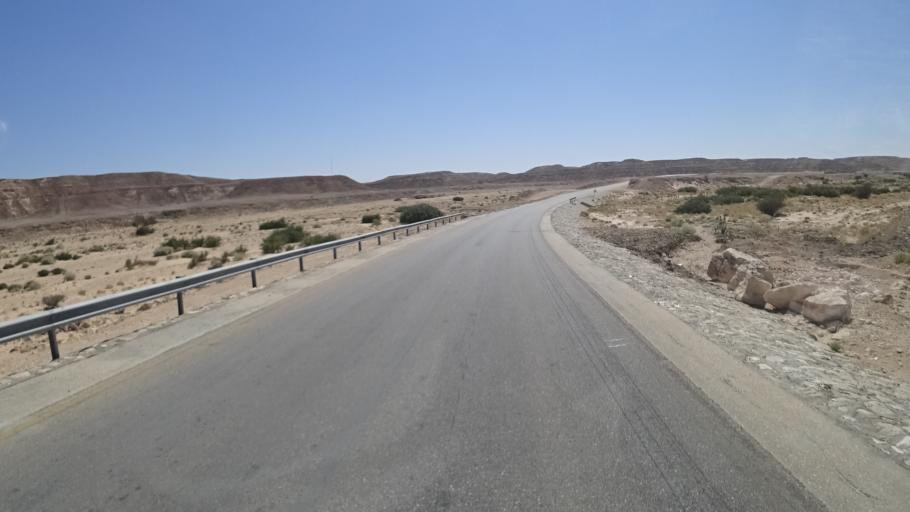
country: OM
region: Zufar
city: Salalah
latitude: 17.4958
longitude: 53.3624
